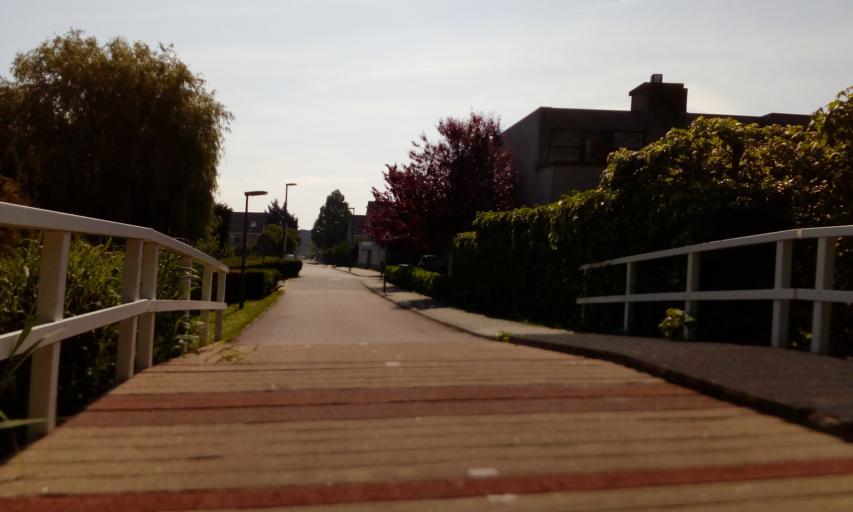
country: NL
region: South Holland
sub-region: Gemeente Rotterdam
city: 's-Gravenland
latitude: 51.9253
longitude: 4.5277
